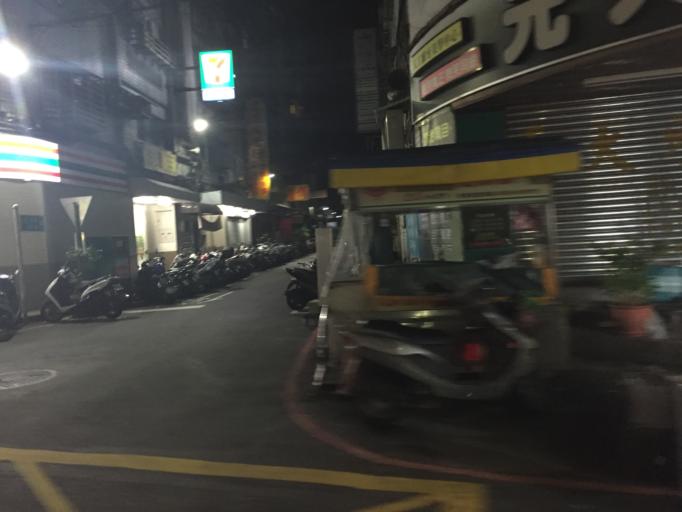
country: TW
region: Taipei
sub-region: Taipei
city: Banqiao
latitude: 25.0828
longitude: 121.4682
